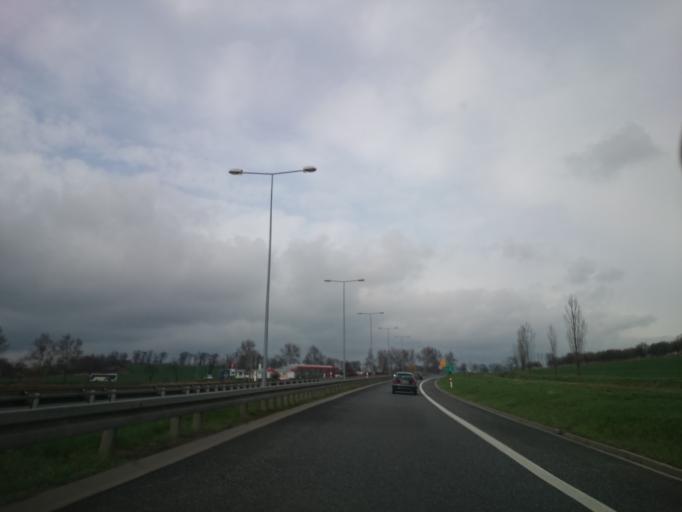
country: PL
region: Opole Voivodeship
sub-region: Powiat nyski
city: Otmuchow
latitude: 50.4647
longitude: 17.1991
